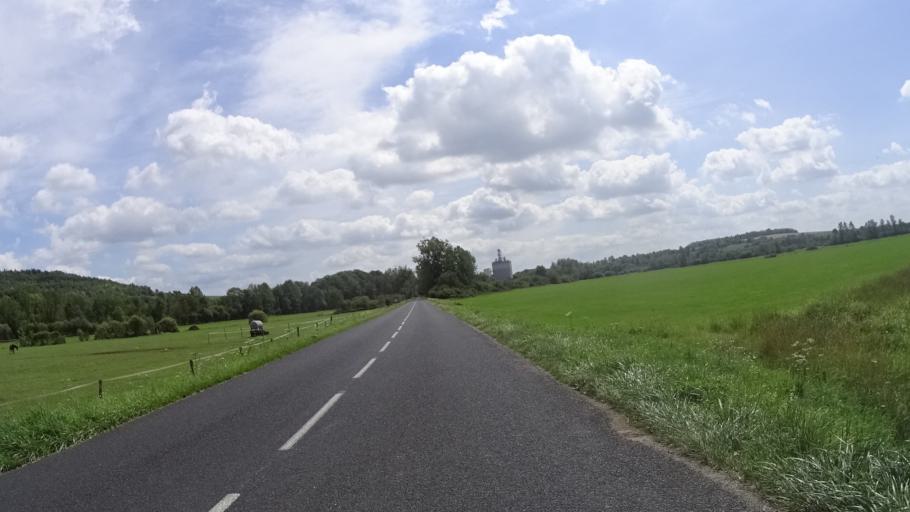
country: FR
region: Lorraine
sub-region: Departement de la Meuse
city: Euville
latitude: 48.7285
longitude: 5.6635
